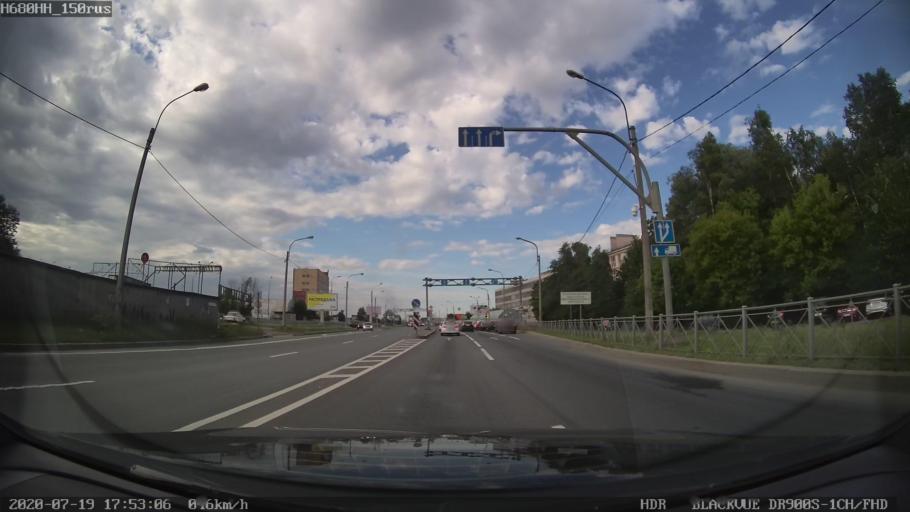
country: RU
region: St.-Petersburg
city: Avtovo
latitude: 59.8745
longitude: 30.2982
